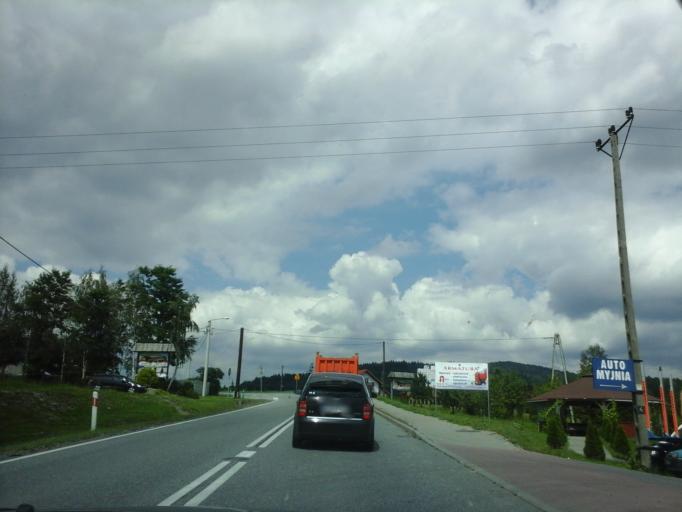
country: PL
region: Lesser Poland Voivodeship
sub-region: Powiat suski
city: Jordanow
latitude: 49.6524
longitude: 19.8200
